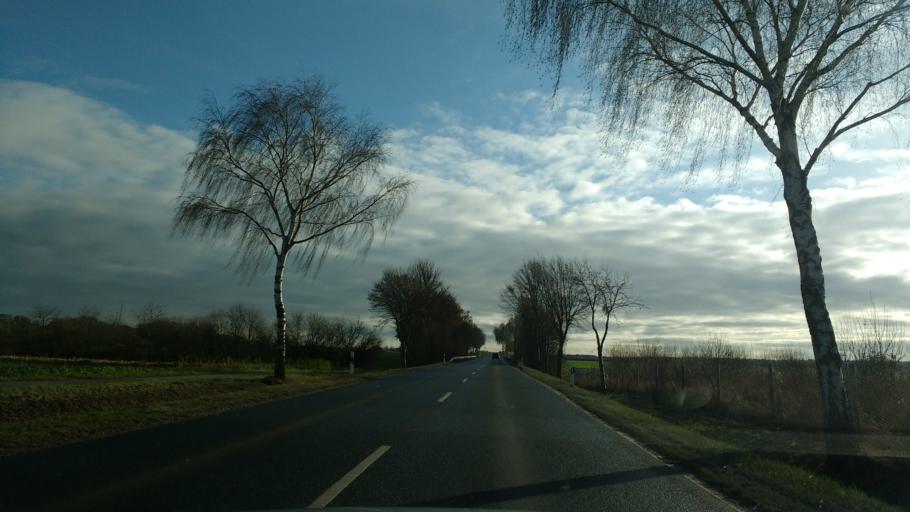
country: DE
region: North Rhine-Westphalia
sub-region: Regierungsbezirk Detmold
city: Salzkotten
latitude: 51.7003
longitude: 8.6761
